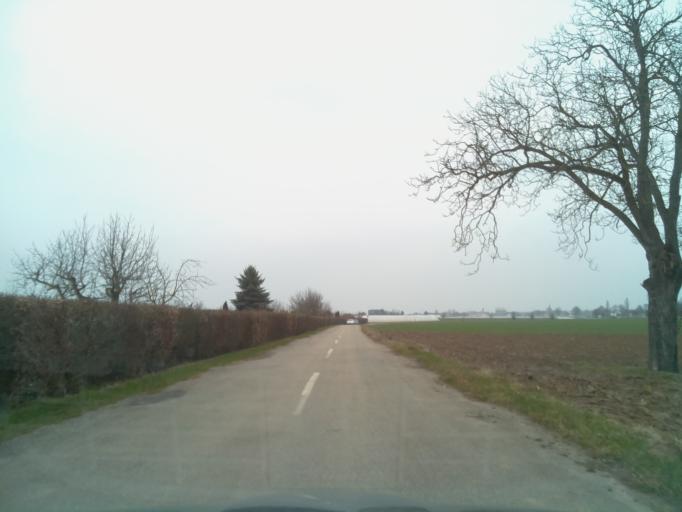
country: DE
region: Baden-Wuerttemberg
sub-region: Karlsruhe Region
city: Ladenburg
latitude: 49.4859
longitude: 8.6010
